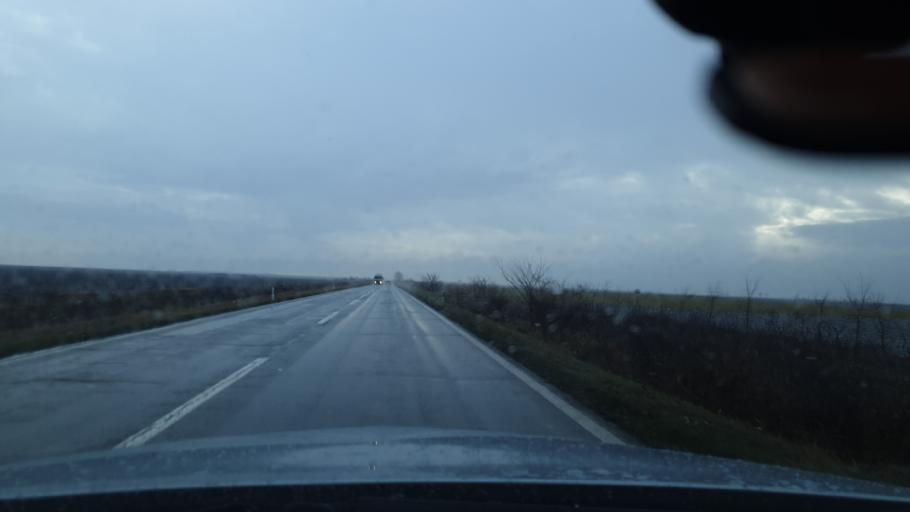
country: RS
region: Autonomna Pokrajina Vojvodina
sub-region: Juznobanatski Okrug
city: Pancevo
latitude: 44.8429
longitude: 20.7932
